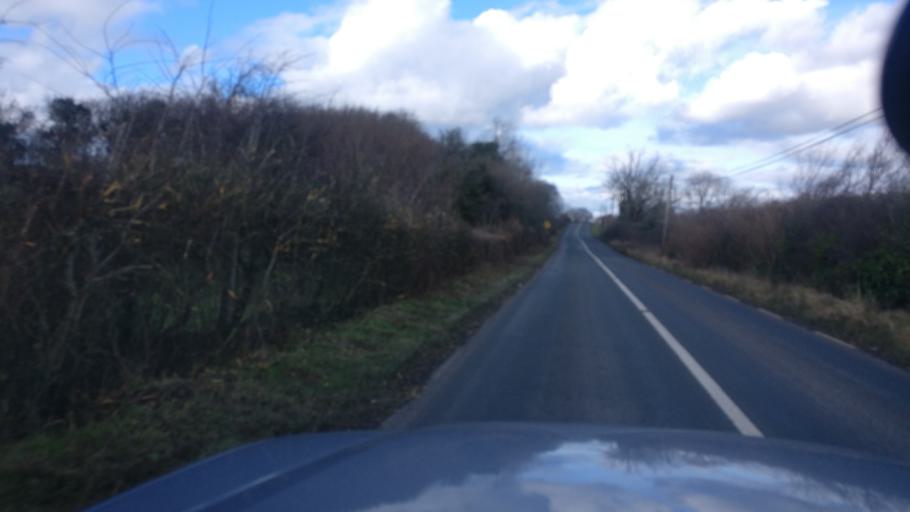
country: IE
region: Connaught
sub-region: County Galway
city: Loughrea
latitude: 53.1599
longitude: -8.3891
